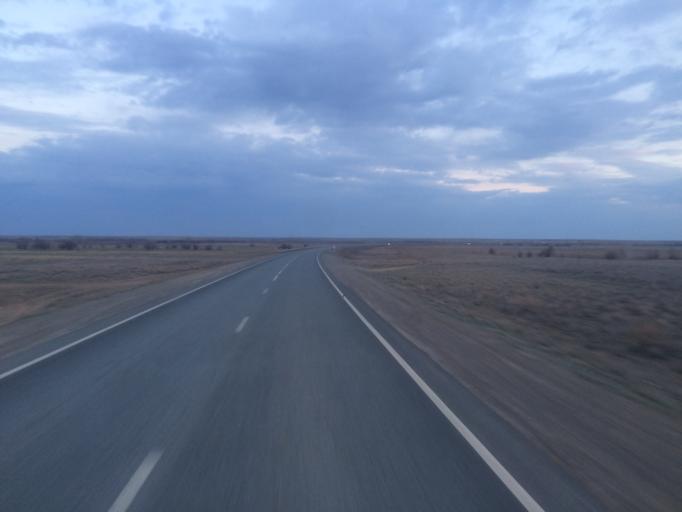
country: KZ
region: Aqtoebe
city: Martuk
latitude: 50.7162
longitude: 56.4828
